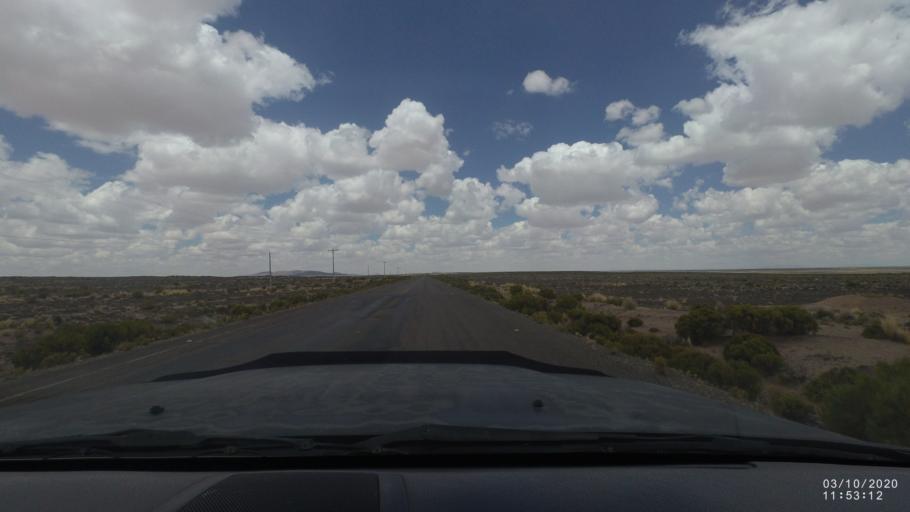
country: BO
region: Oruro
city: Poopo
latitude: -18.4735
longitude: -67.6029
